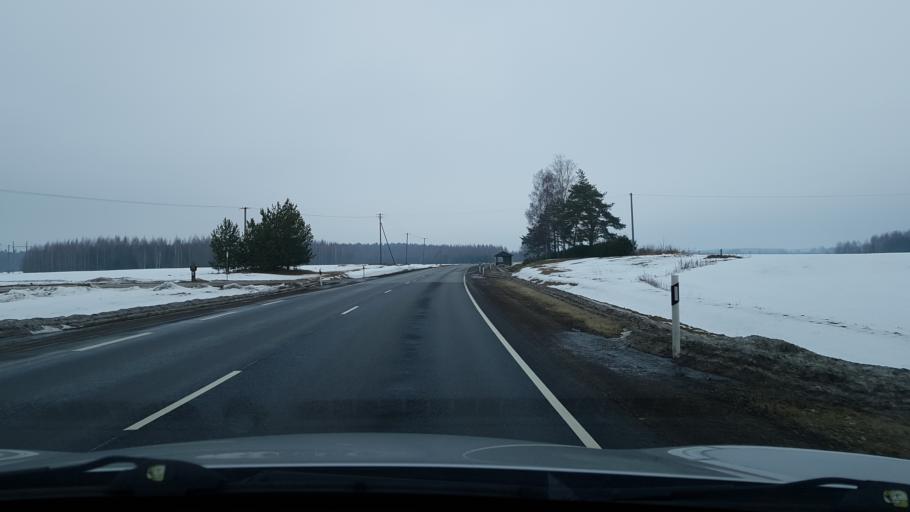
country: EE
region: Valgamaa
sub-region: Valga linn
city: Valga
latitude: 57.8982
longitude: 26.1681
